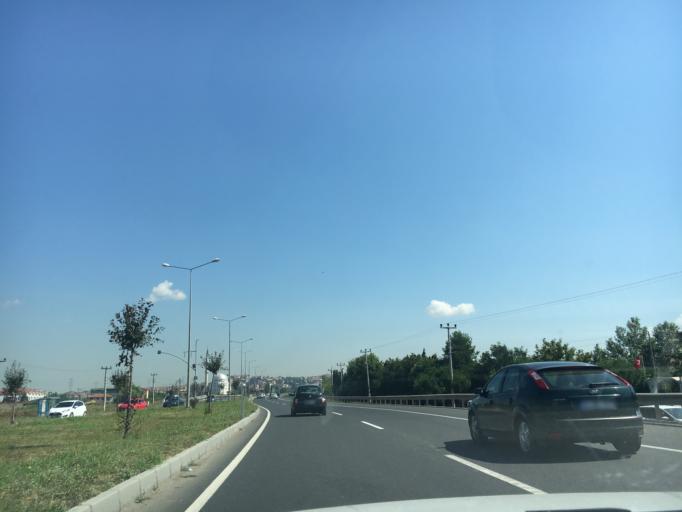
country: TR
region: Tekirdag
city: Sultankoy
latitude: 41.0092
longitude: 27.9813
